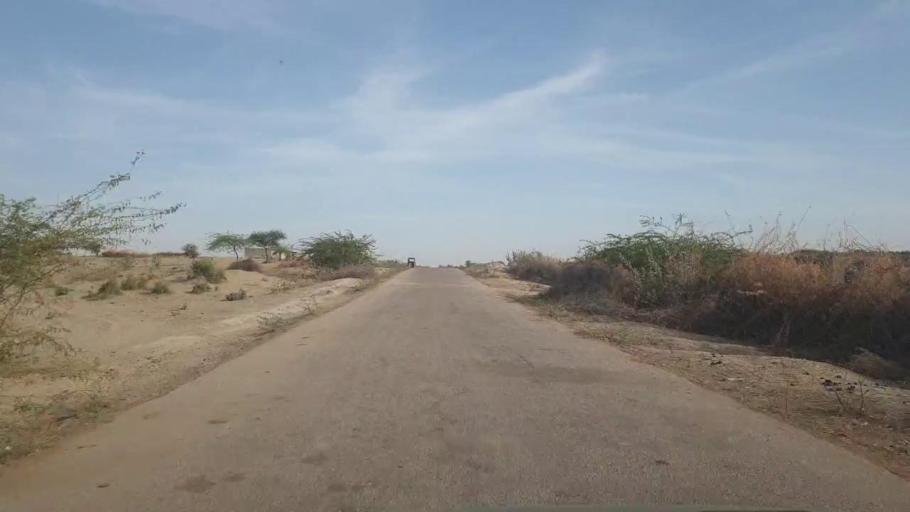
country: PK
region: Sindh
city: Nabisar
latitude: 25.0681
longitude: 69.6476
